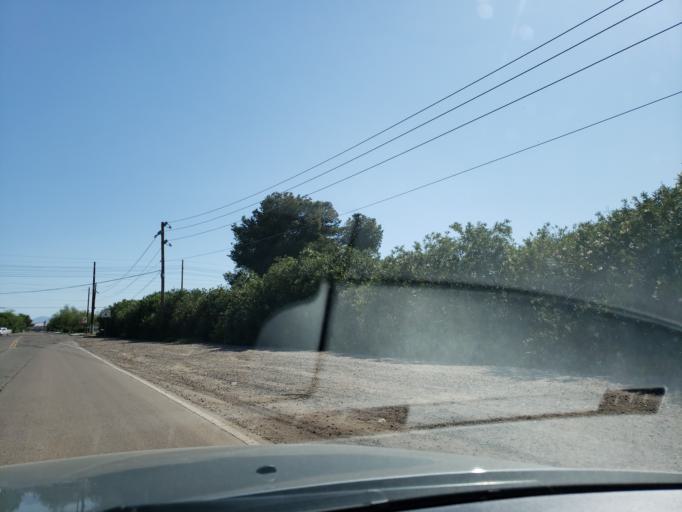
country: US
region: Arizona
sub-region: Maricopa County
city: Glendale
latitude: 33.5543
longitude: -112.1950
